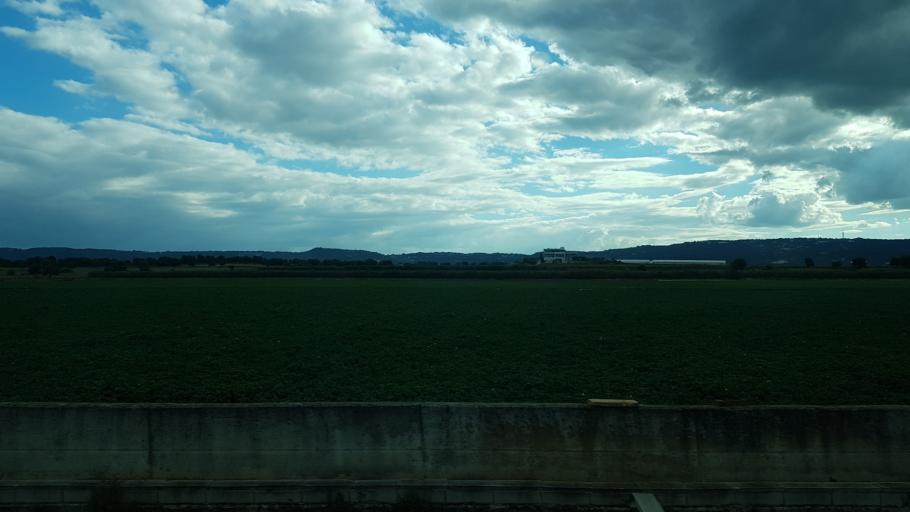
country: IT
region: Apulia
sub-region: Provincia di Brindisi
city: Fasano
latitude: 40.8461
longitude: 17.3941
